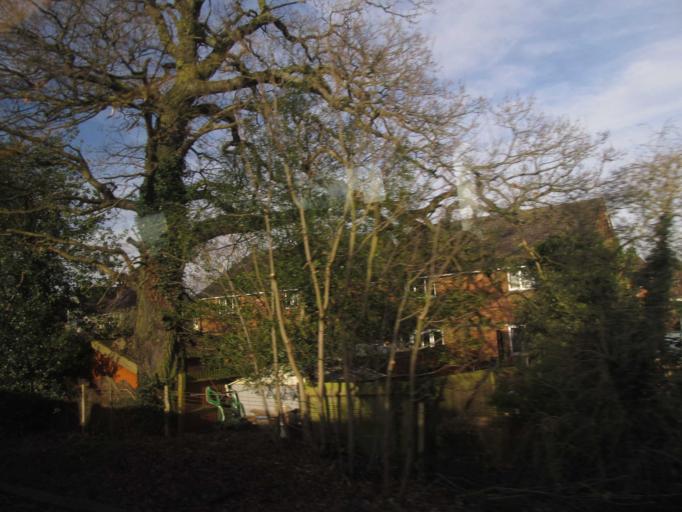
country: GB
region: England
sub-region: Surrey
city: Godalming
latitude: 51.2004
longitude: -0.5996
